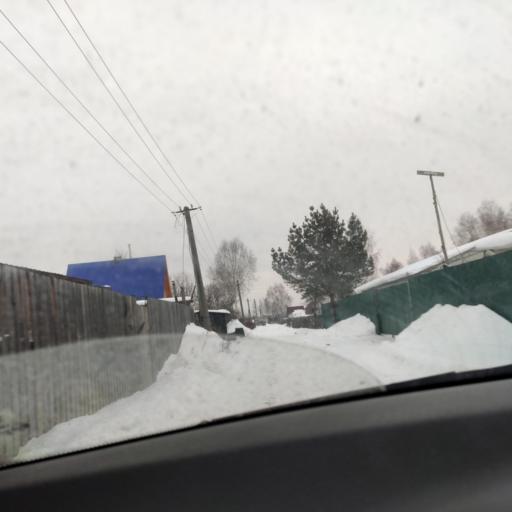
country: RU
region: Perm
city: Kondratovo
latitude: 57.9583
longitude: 56.0828
